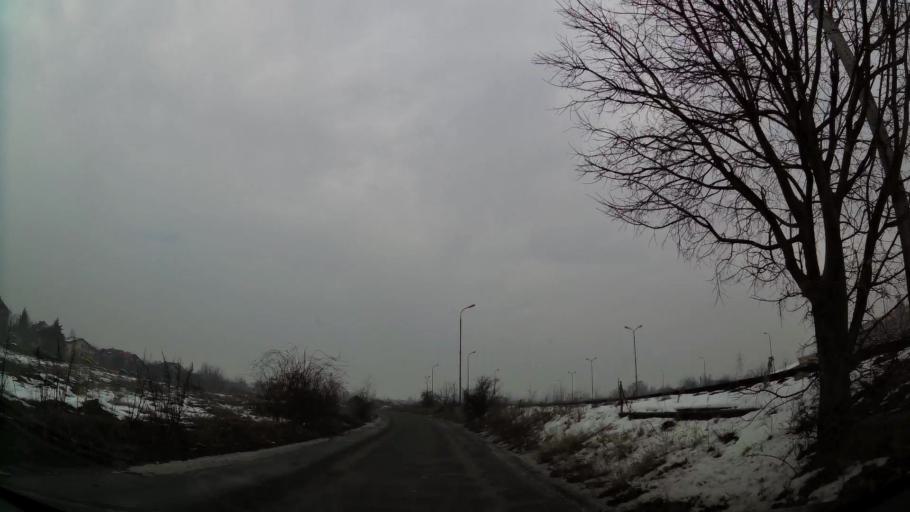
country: MK
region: Saraj
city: Saraj
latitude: 42.0159
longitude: 21.3621
